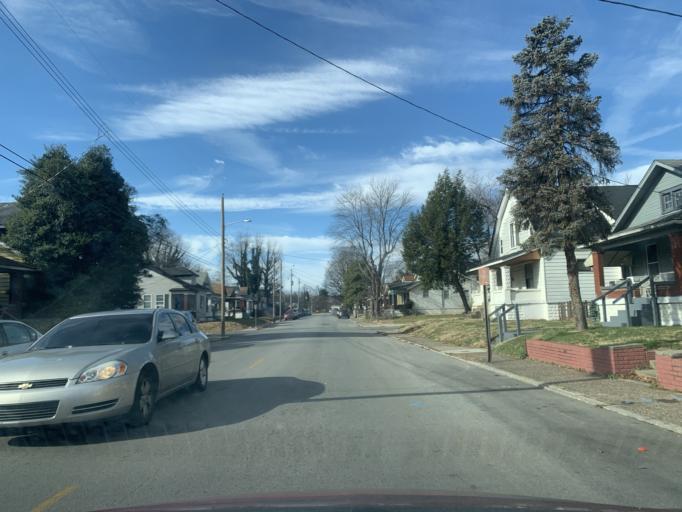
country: US
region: Kentucky
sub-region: Jefferson County
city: Shively
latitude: 38.2294
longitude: -85.7947
